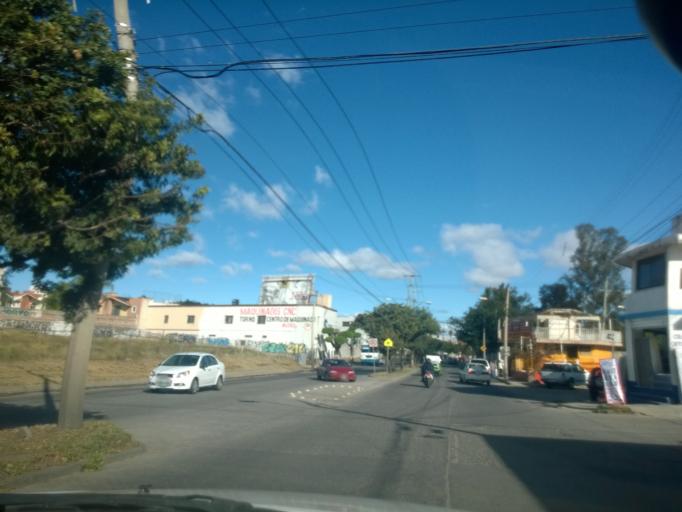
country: MX
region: Guanajuato
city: Leon
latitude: 21.1172
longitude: -101.7039
